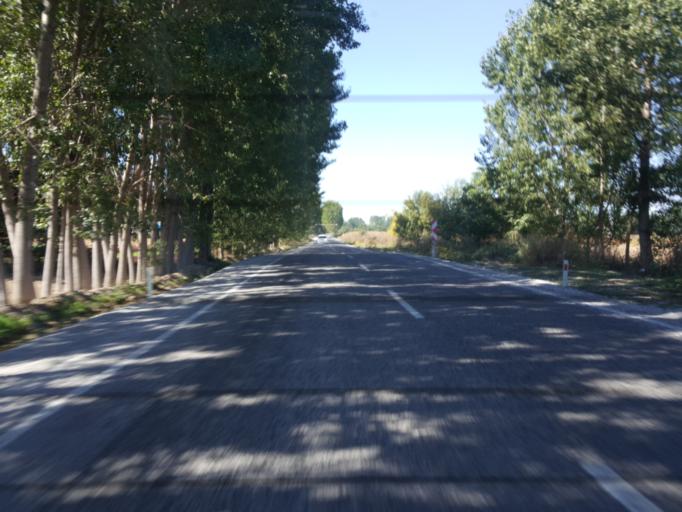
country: TR
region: Tokat
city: Pazar
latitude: 40.2691
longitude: 36.2211
